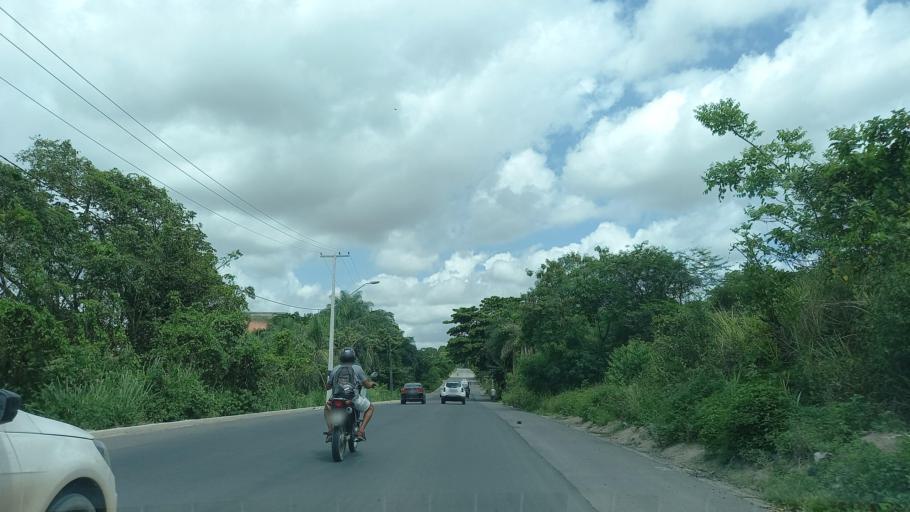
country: BR
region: Pernambuco
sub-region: Jaboatao Dos Guararapes
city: Jaboatao dos Guararapes
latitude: -8.1430
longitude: -35.0009
